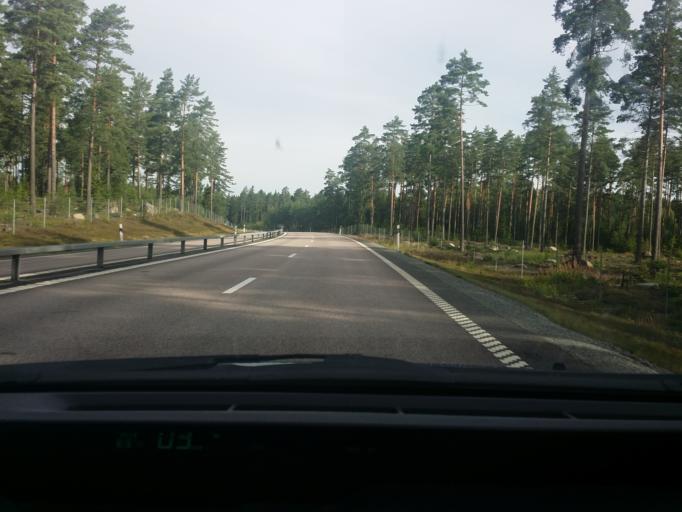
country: SE
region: Vaestmanland
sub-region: Sala Kommun
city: Sala
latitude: 59.8101
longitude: 16.5531
